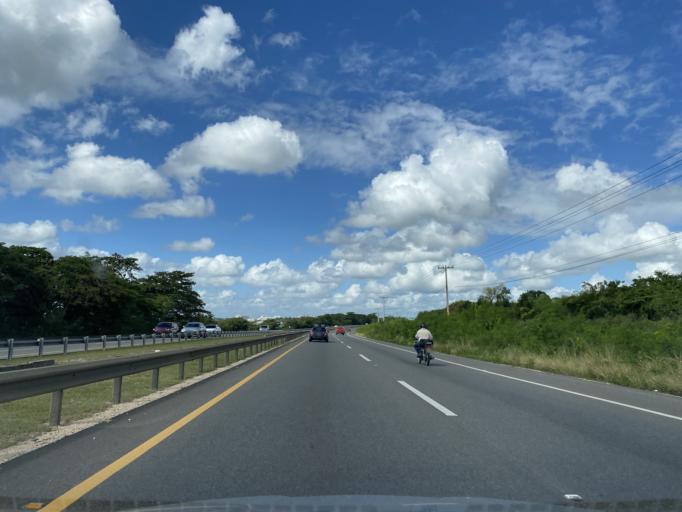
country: DO
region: Santo Domingo
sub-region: Santo Domingo
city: Boca Chica
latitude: 18.4435
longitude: -69.5845
